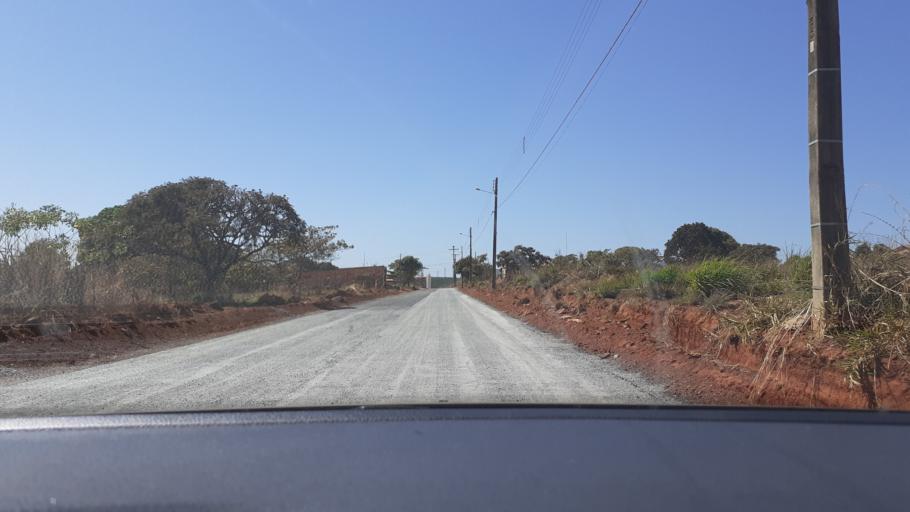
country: BR
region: Goias
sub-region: Aparecida De Goiania
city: Aparecida de Goiania
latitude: -16.8779
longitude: -49.2562
